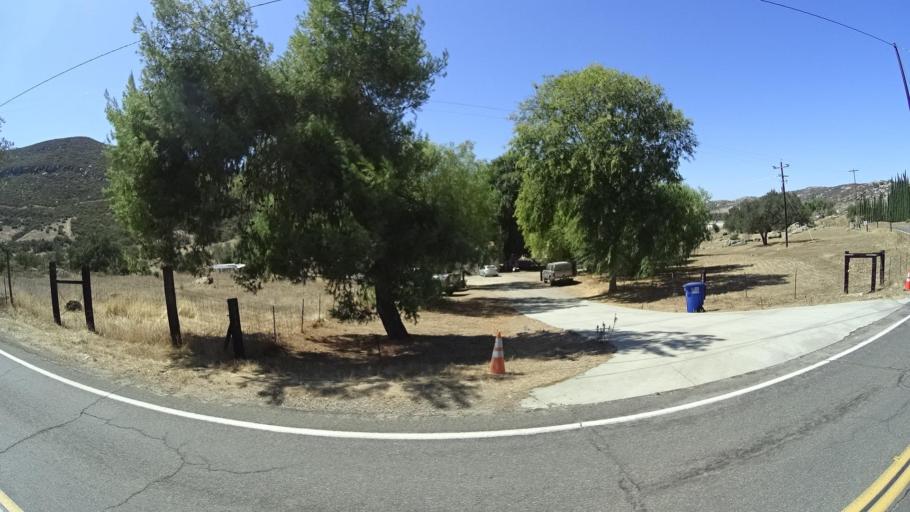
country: US
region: California
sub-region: San Diego County
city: San Diego Country Estates
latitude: 33.0506
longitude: -116.7952
